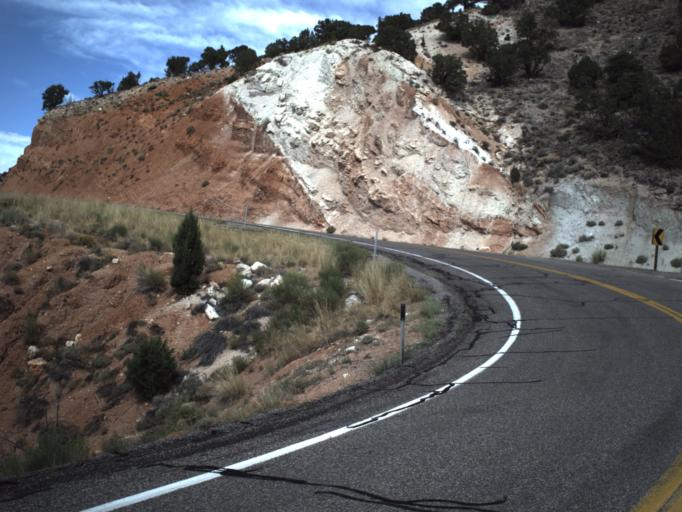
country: US
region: Utah
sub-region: Sevier County
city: Richfield
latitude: 38.7741
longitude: -111.9465
